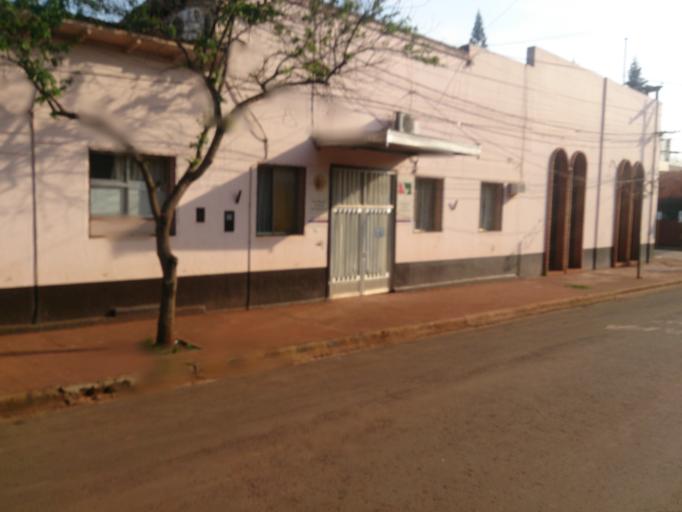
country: AR
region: Misiones
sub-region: Departamento de Obera
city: Obera
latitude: -27.4842
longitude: -55.1215
